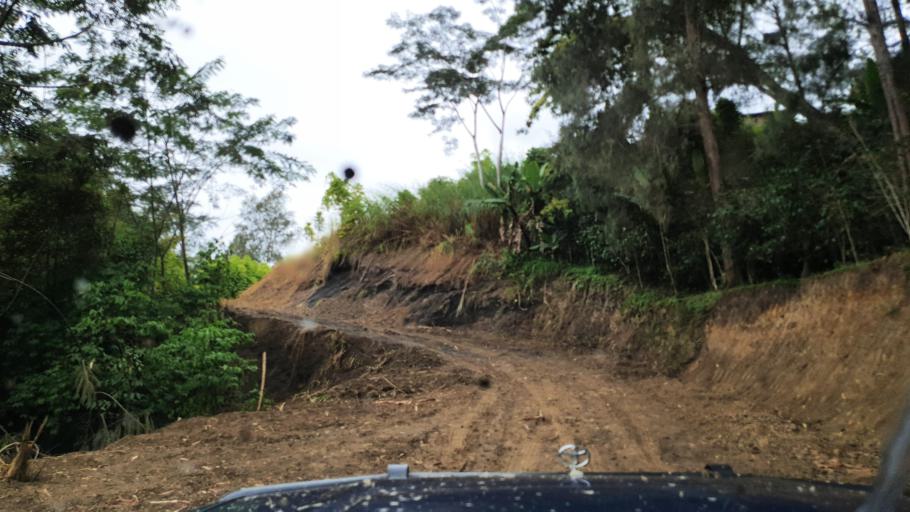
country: PG
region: Jiwaka
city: Minj
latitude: -5.9284
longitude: 144.7420
